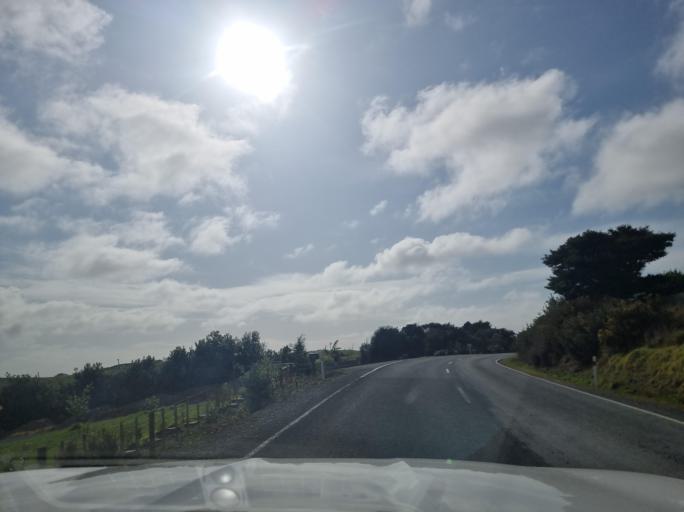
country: NZ
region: Northland
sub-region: Whangarei
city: Ruakaka
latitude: -36.0136
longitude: 174.4644
